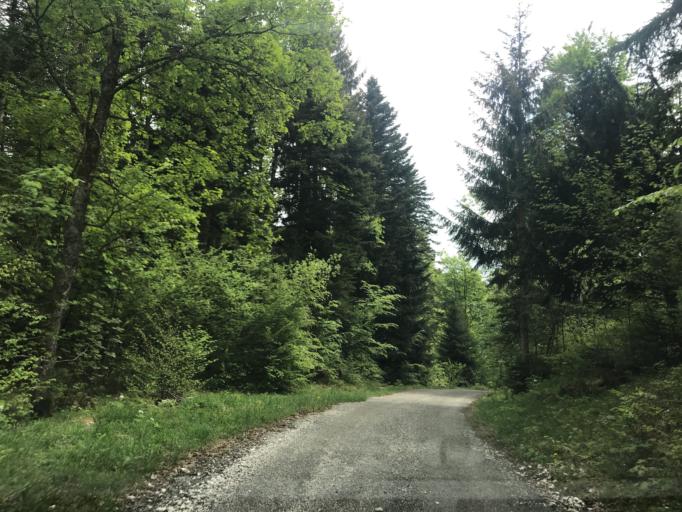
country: FR
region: Rhone-Alpes
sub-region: Departement de la Savoie
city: La Motte-Servolex
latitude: 45.6016
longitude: 5.8223
